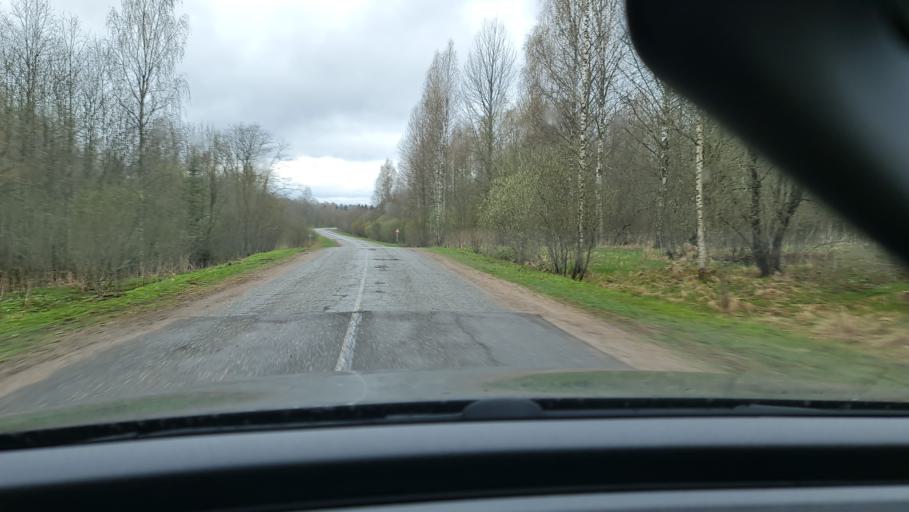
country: RU
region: Novgorod
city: Marevo
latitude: 57.2470
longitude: 32.0658
